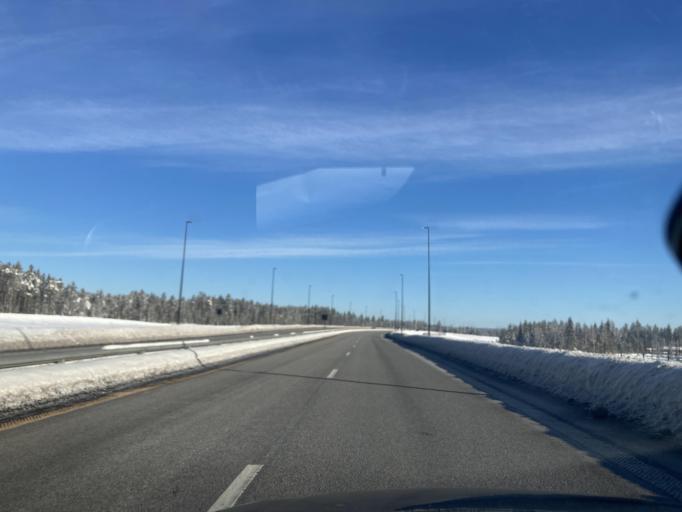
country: NO
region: Hedmark
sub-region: Loten
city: Loten
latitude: 60.8721
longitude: 11.4431
